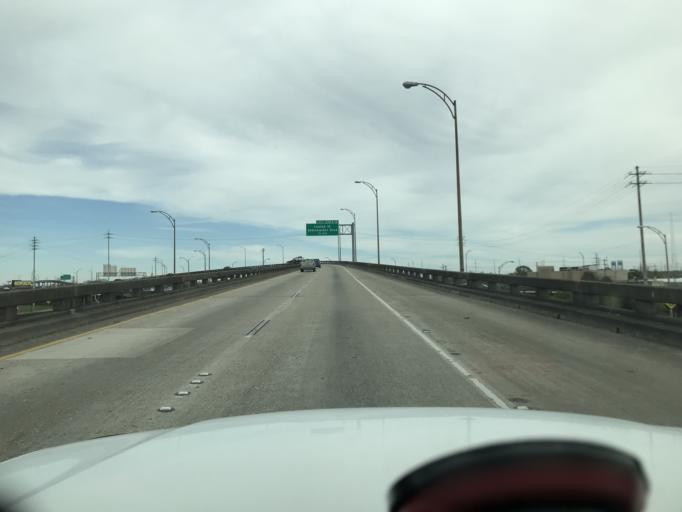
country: US
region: Louisiana
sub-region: Orleans Parish
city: New Orleans
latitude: 29.9913
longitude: -90.0517
